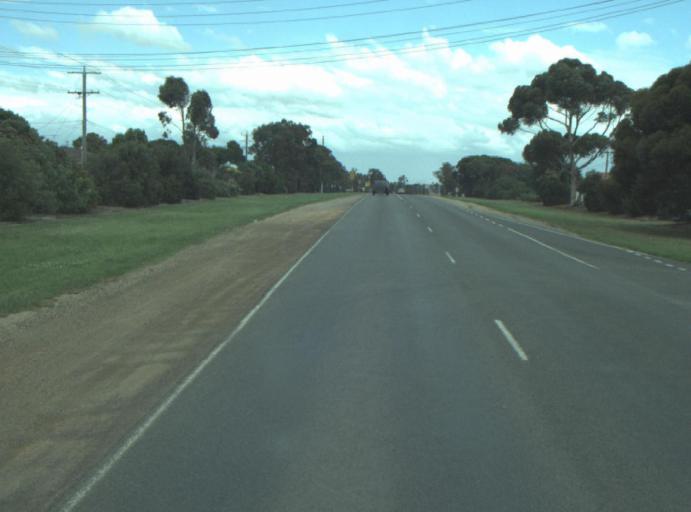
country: AU
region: Victoria
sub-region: Greater Geelong
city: Bell Park
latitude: -38.0682
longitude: 144.3587
